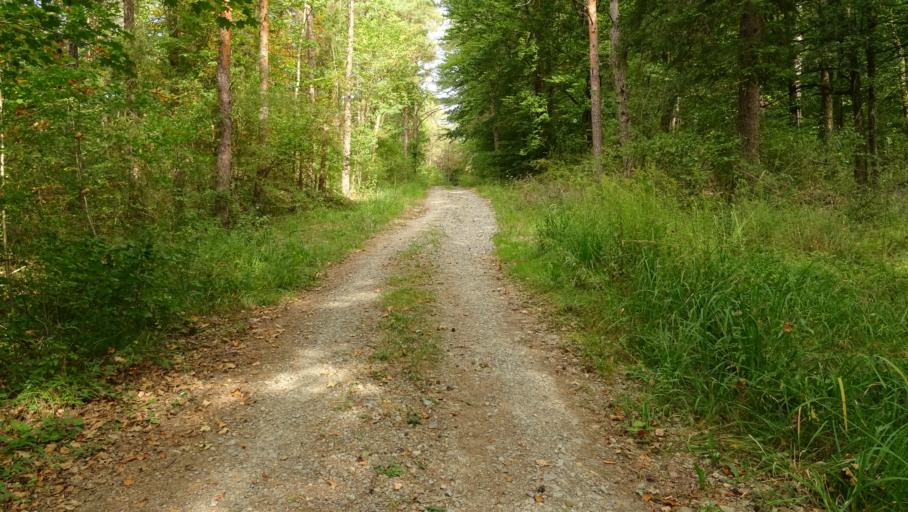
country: DE
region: Baden-Wuerttemberg
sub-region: Karlsruhe Region
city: Mosbach
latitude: 49.3842
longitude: 9.1589
